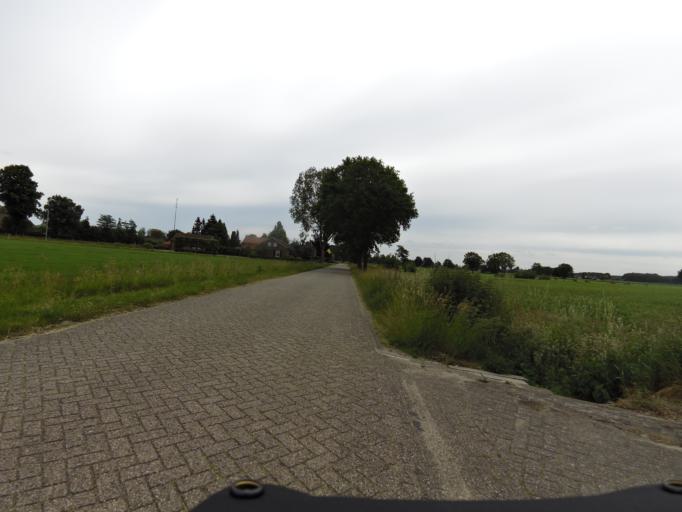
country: NL
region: North Brabant
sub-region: Gemeente Hilvarenbeek
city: Hilvarenbeek
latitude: 51.4868
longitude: 5.1081
